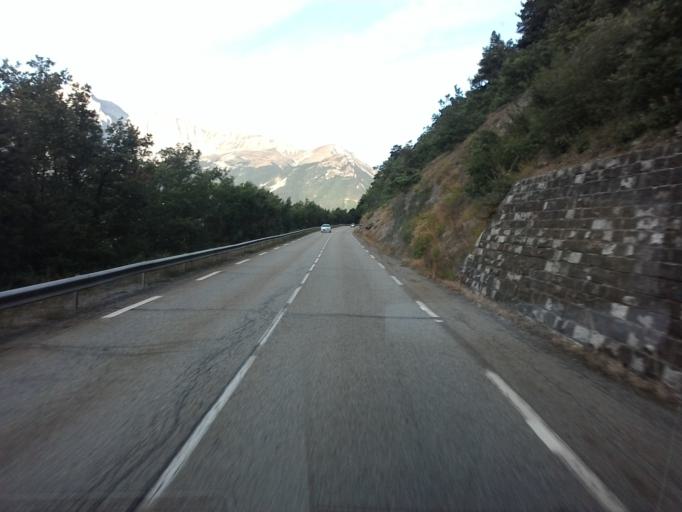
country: FR
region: Rhone-Alpes
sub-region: Departement de l'Isere
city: La Mure
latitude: 44.8330
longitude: 5.9010
